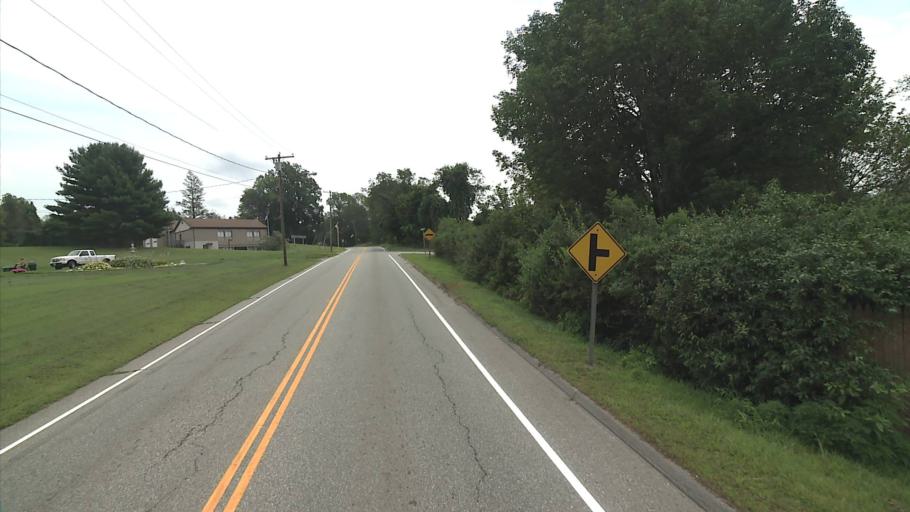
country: US
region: Connecticut
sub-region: Windham County
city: Wauregan
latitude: 41.7445
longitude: -71.9102
